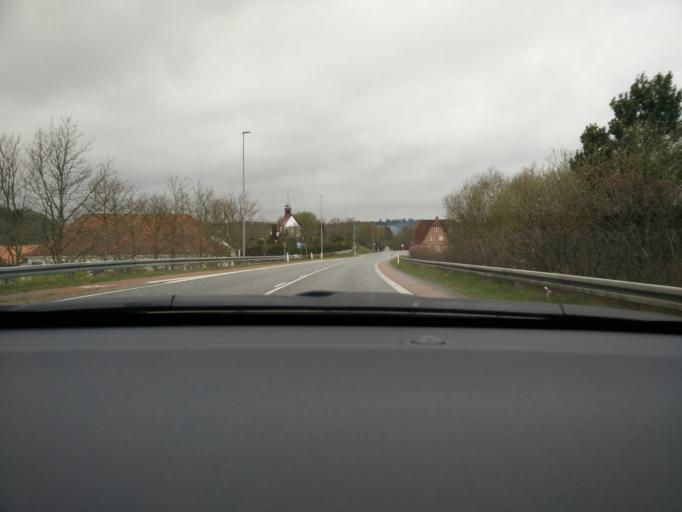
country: DK
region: Central Jutland
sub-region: Viborg Kommune
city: Viborg
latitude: 56.5116
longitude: 9.3135
